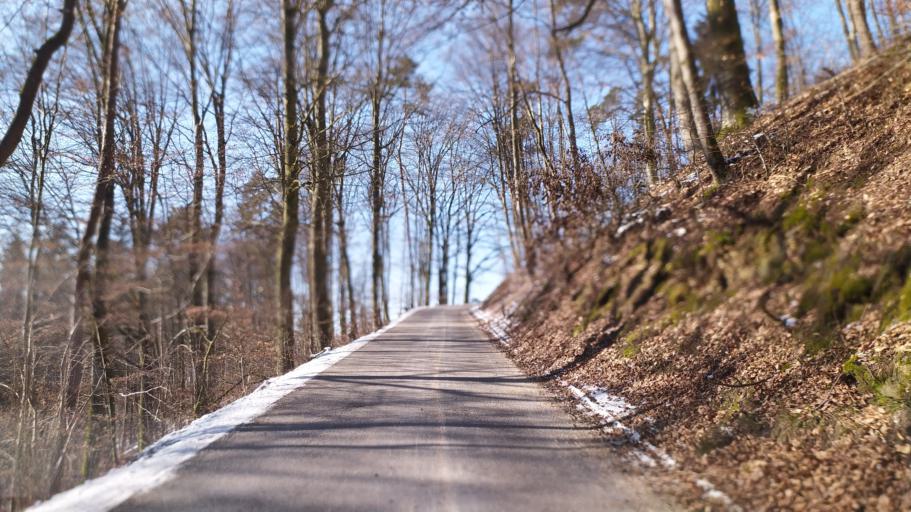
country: AT
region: Upper Austria
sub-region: Politischer Bezirk Urfahr-Umgebung
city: Ottensheim
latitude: 48.3339
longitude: 14.2080
